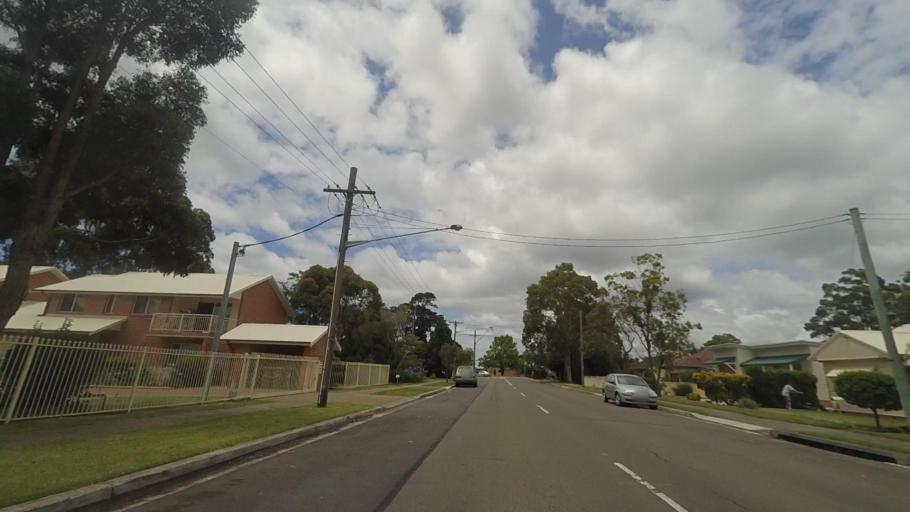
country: AU
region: New South Wales
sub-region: Sutherland Shire
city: Engadine
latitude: -34.0705
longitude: 151.0096
